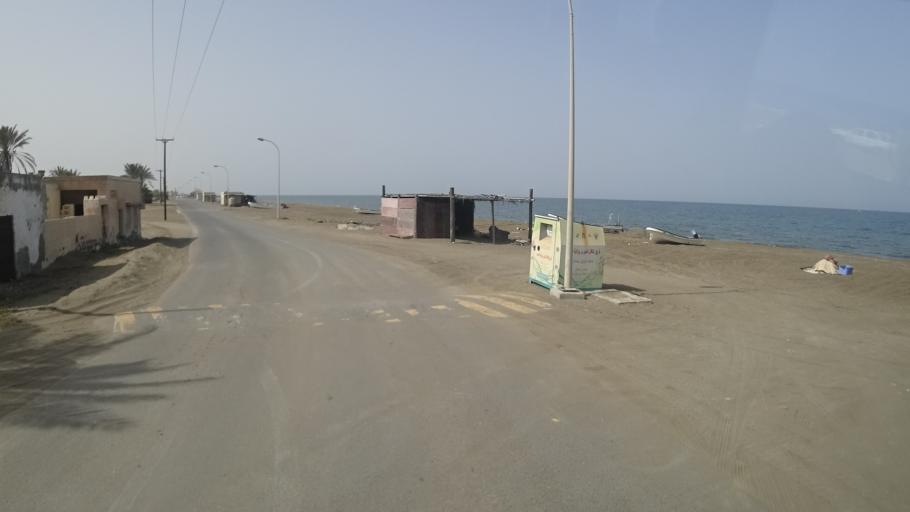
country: OM
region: Al Batinah
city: Saham
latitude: 24.2486
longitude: 56.8326
